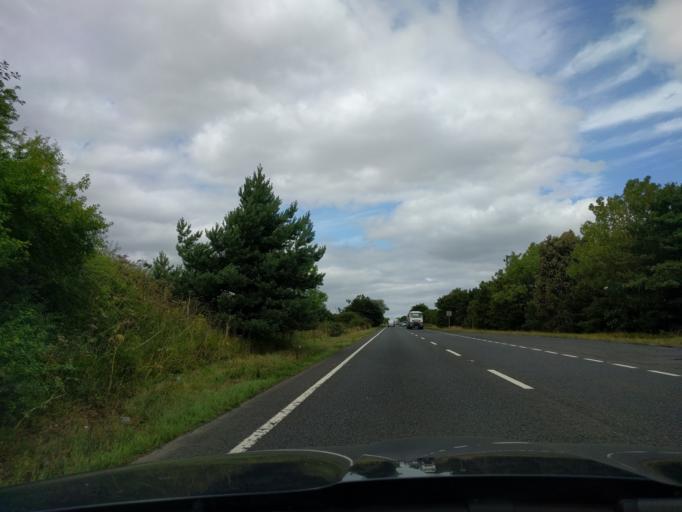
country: GB
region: England
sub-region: Northumberland
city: Alnwick
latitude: 55.4361
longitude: -1.6935
